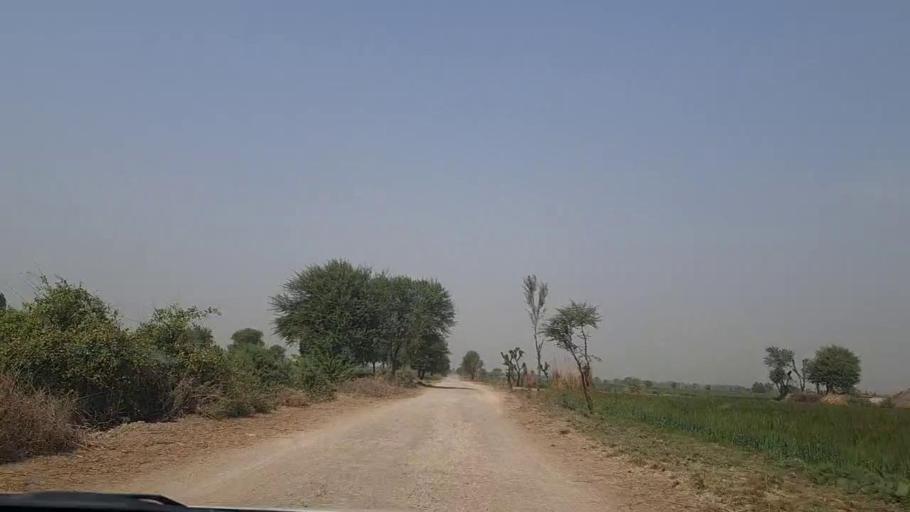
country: PK
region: Sindh
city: Mirpur Khas
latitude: 25.6111
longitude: 69.2010
